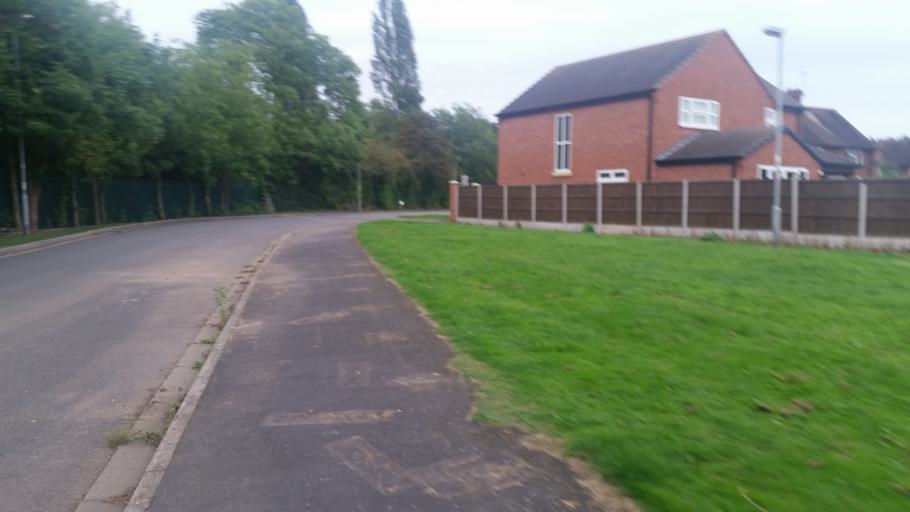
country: GB
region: England
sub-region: Nottinghamshire
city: Ruddington
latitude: 52.8984
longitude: -1.1467
